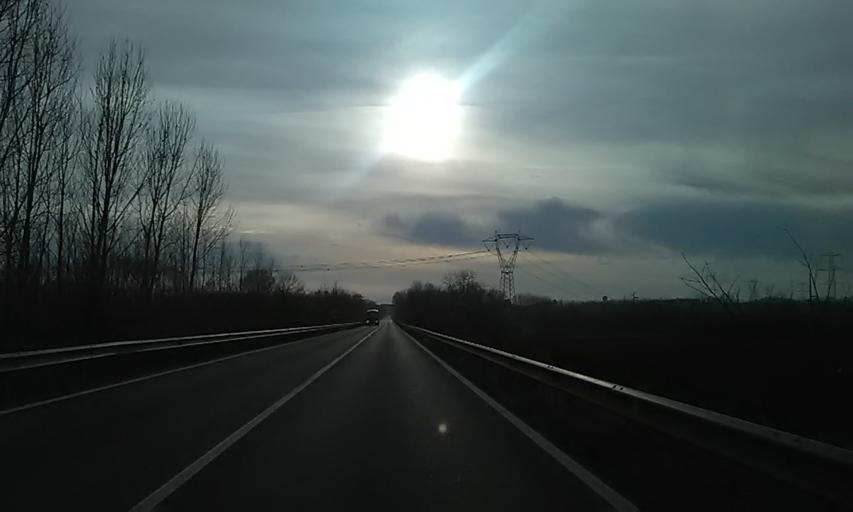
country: IT
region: Piedmont
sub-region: Provincia di Torino
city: Rondissone
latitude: 45.2620
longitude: 7.9740
